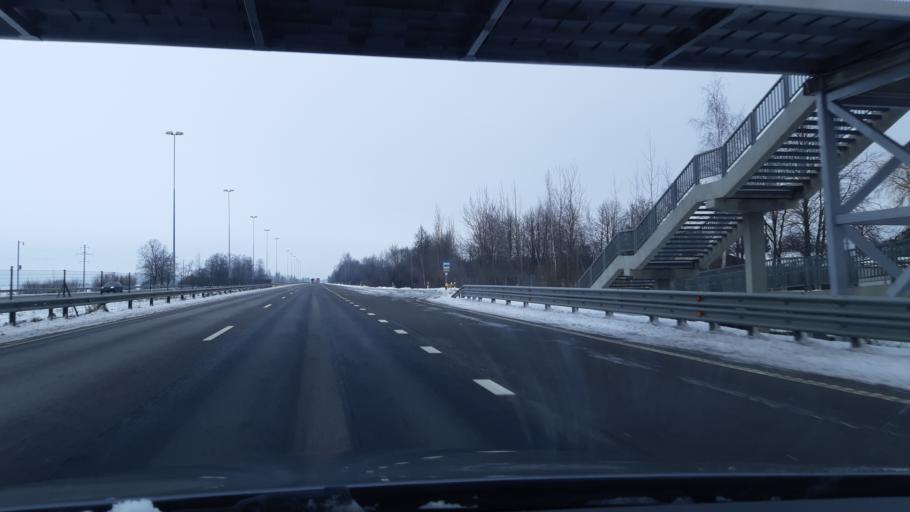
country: LT
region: Kauno apskritis
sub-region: Kaunas
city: Sargenai
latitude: 55.0107
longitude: 23.8373
